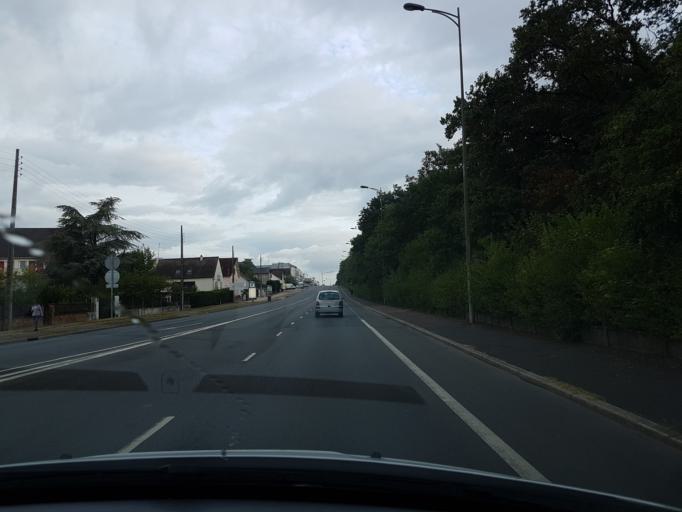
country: FR
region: Centre
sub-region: Departement d'Indre-et-Loire
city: Chambray-les-Tours
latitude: 47.3517
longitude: 0.7001
